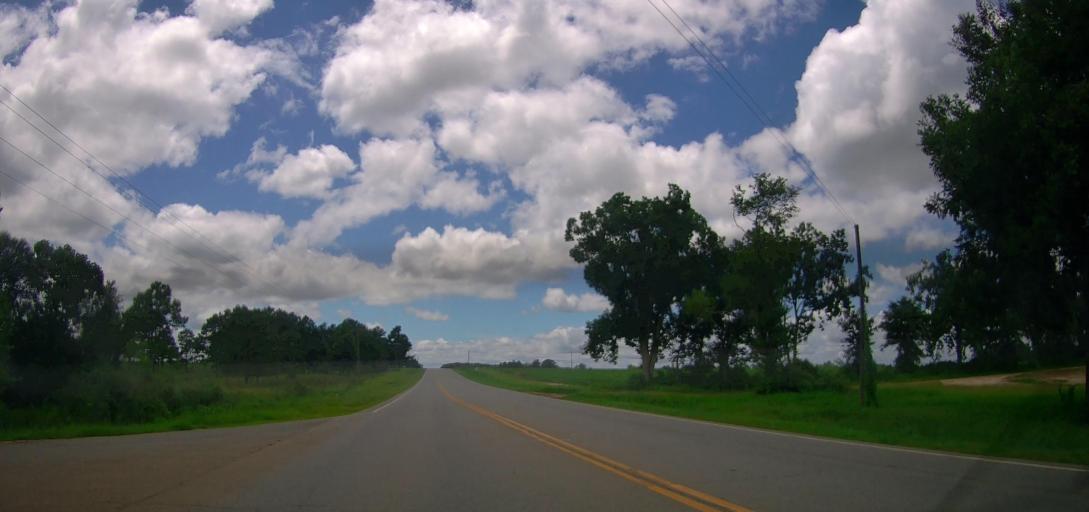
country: US
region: Georgia
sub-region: Turner County
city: Ashburn
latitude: 31.7220
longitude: -83.5388
